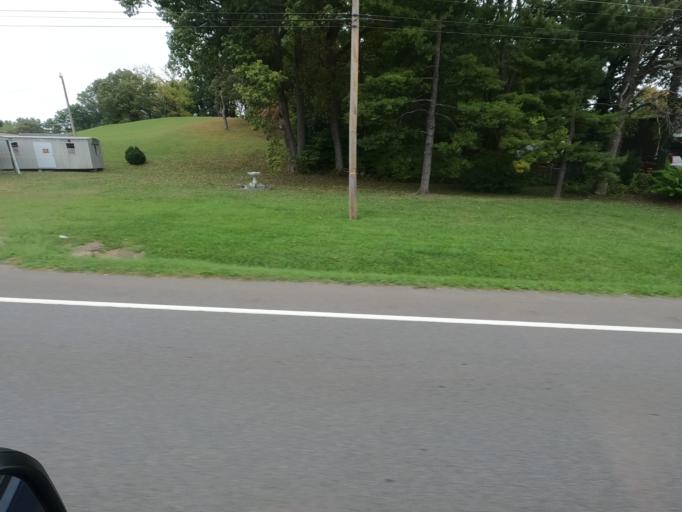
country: US
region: Tennessee
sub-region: Washington County
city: Midway
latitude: 36.3097
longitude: -82.4006
